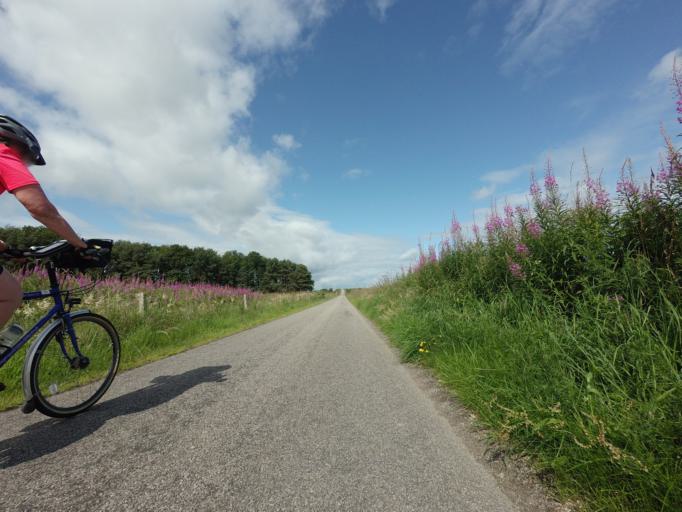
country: GB
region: Scotland
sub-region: Moray
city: Burghead
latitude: 57.6533
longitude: -3.4680
